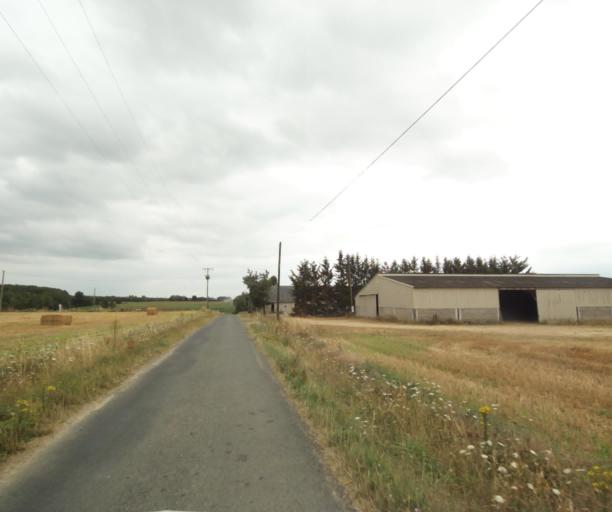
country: FR
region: Pays de la Loire
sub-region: Departement de la Sarthe
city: Sable-sur-Sarthe
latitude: 47.8081
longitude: -0.3794
